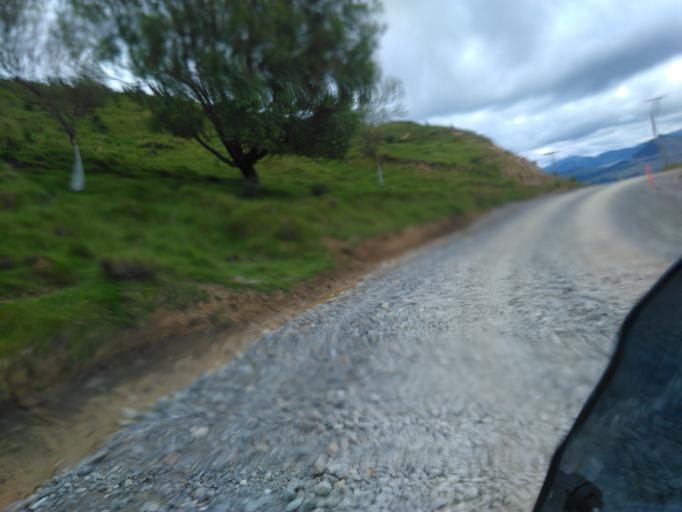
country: NZ
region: Gisborne
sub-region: Gisborne District
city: Gisborne
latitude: -38.0952
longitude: 178.0985
